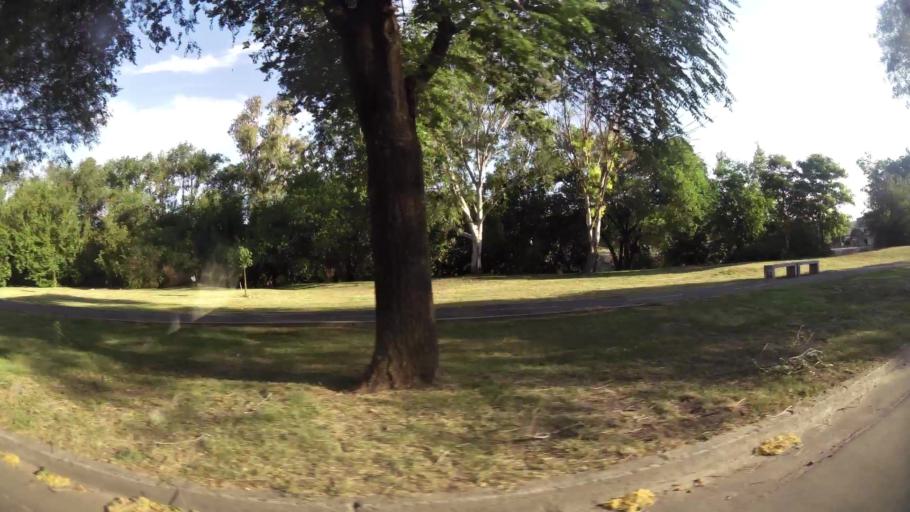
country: AR
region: Cordoba
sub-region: Departamento de Capital
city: Cordoba
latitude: -31.3949
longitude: -64.2196
